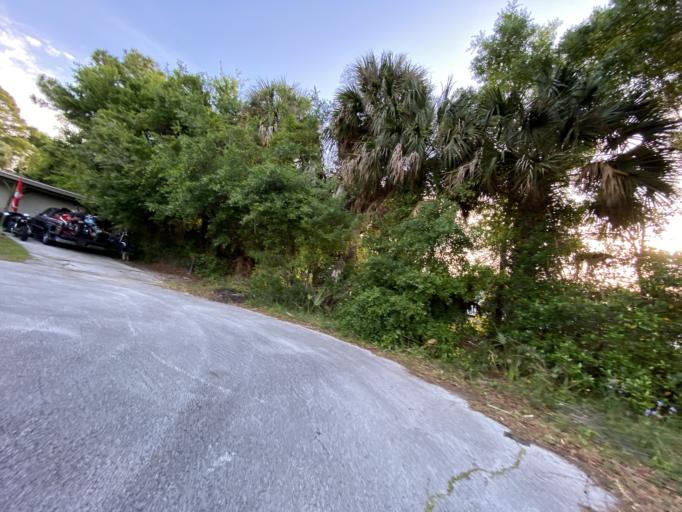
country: US
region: Florida
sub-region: Volusia County
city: South Daytona
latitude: 29.1754
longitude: -81.0082
